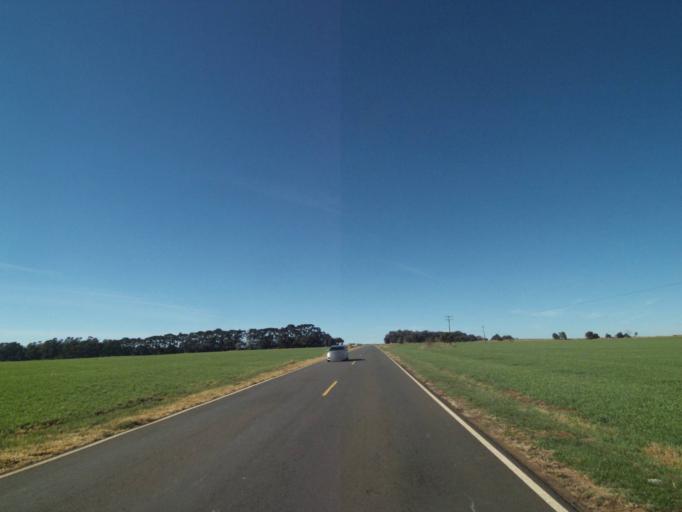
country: BR
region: Parana
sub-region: Tibagi
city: Tibagi
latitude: -24.5475
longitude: -50.2971
